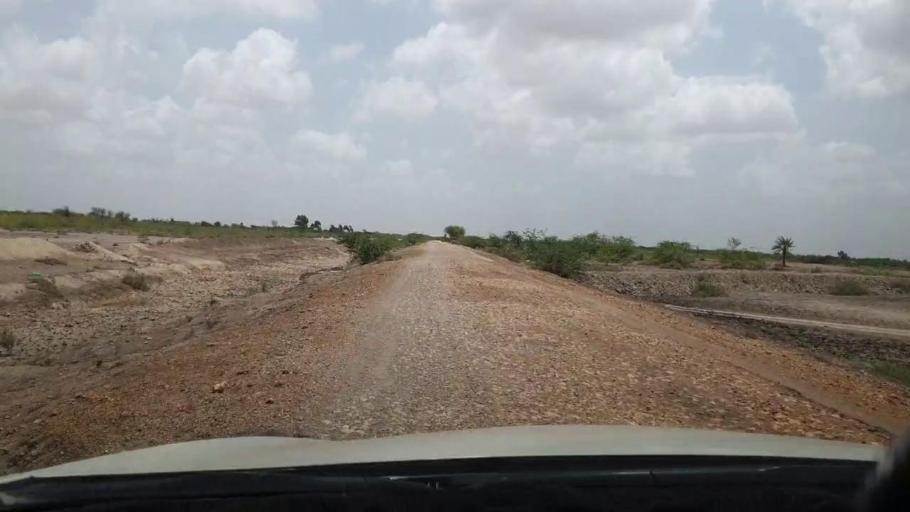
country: PK
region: Sindh
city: Kadhan
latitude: 24.3901
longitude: 68.9344
